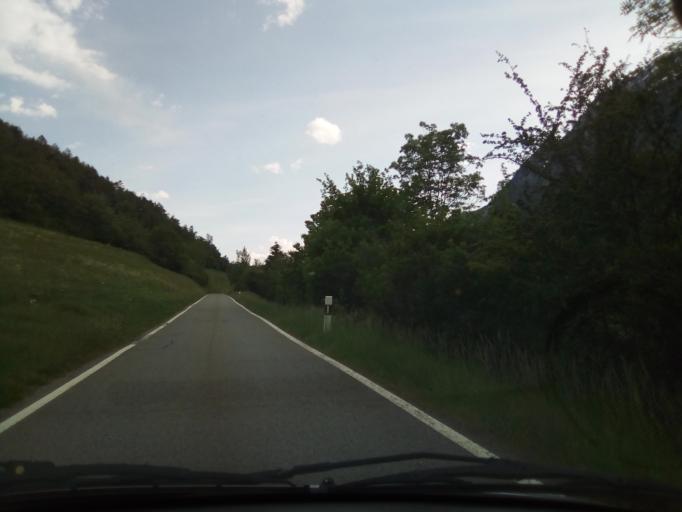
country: CH
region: Valais
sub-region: Entremont District
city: Orsieres
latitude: 46.0679
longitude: 7.1561
